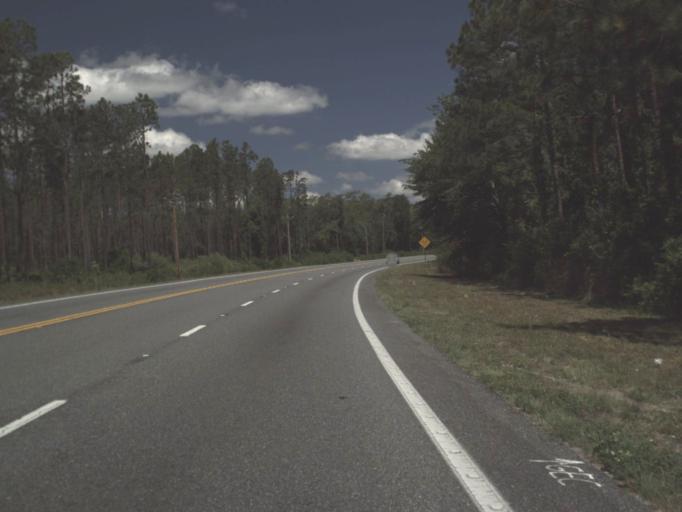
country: US
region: Florida
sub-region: Marion County
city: Silver Springs Shores
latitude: 29.1872
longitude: -81.9042
